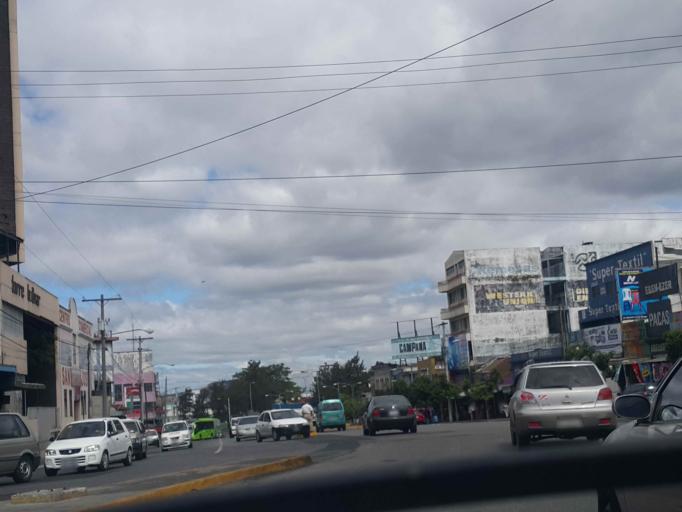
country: GT
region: Guatemala
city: Guatemala City
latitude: 14.6287
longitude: -90.5189
